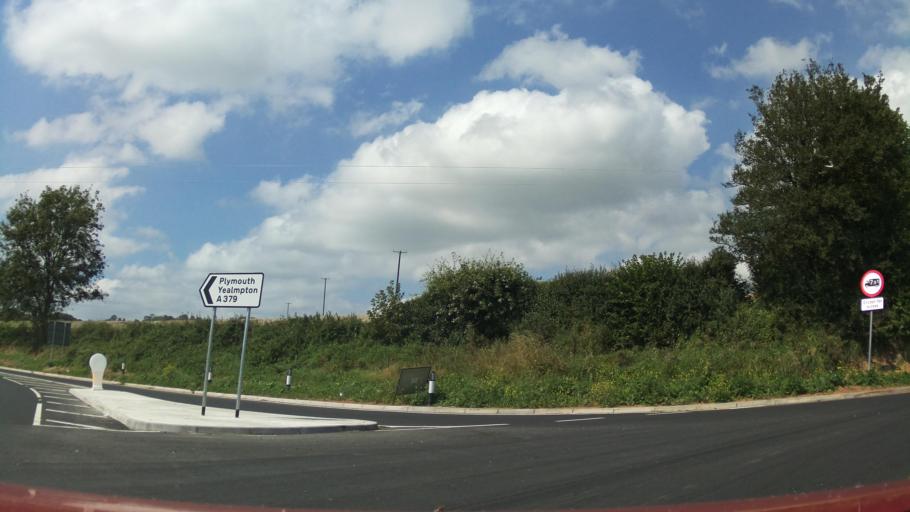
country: GB
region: England
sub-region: Devon
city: Ivybridge
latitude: 50.3540
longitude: -3.9286
